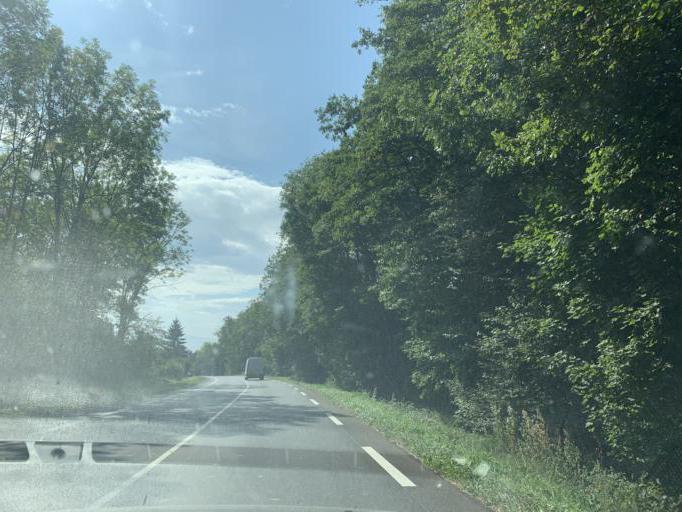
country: FR
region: Rhone-Alpes
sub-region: Departement de l'Ain
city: Divonne-les-Bains
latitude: 46.3533
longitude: 6.1305
